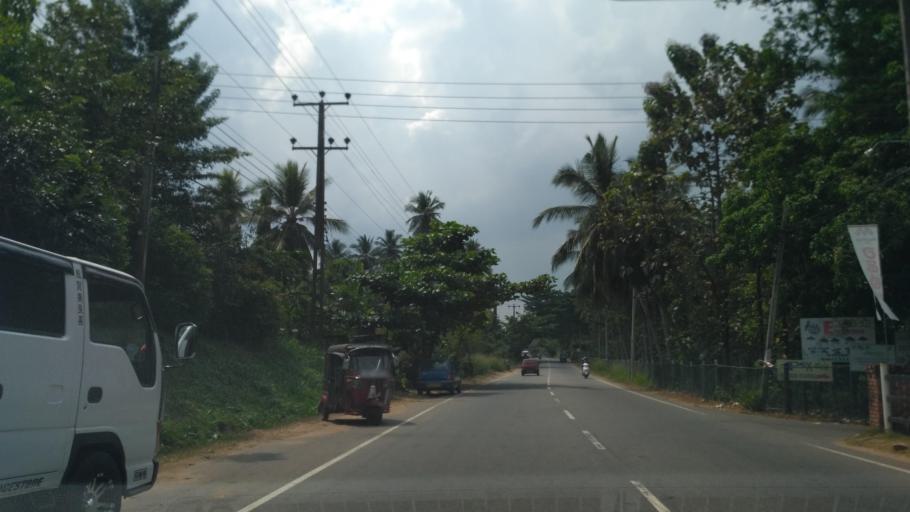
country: LK
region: North Western
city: Kuliyapitiya
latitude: 7.3270
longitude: 80.1171
